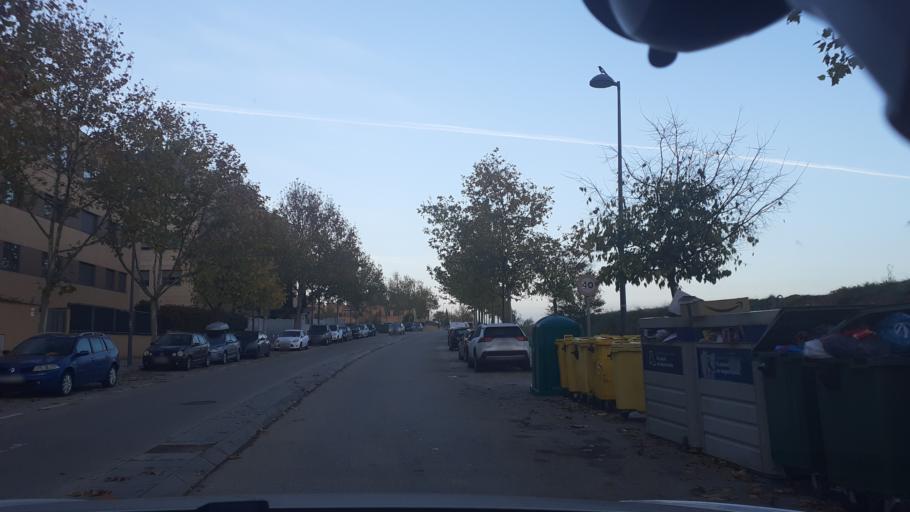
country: ES
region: Madrid
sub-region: Provincia de Madrid
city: Paracuellos de Jarama
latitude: 40.5054
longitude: -3.5077
